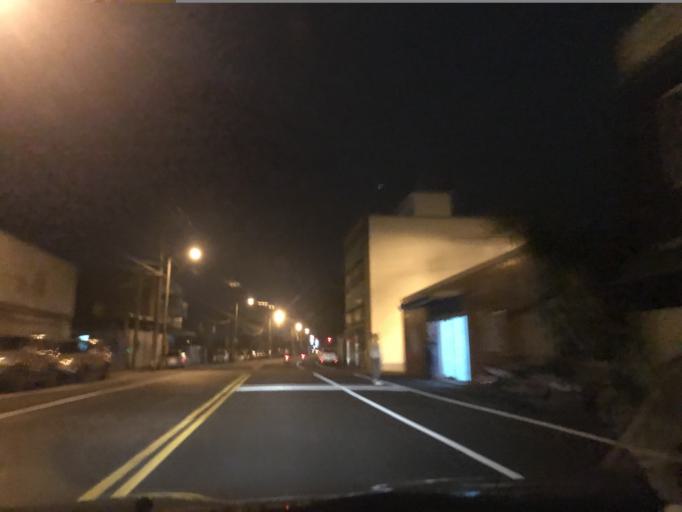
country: TW
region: Taiwan
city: Taoyuan City
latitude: 24.9427
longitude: 121.2434
